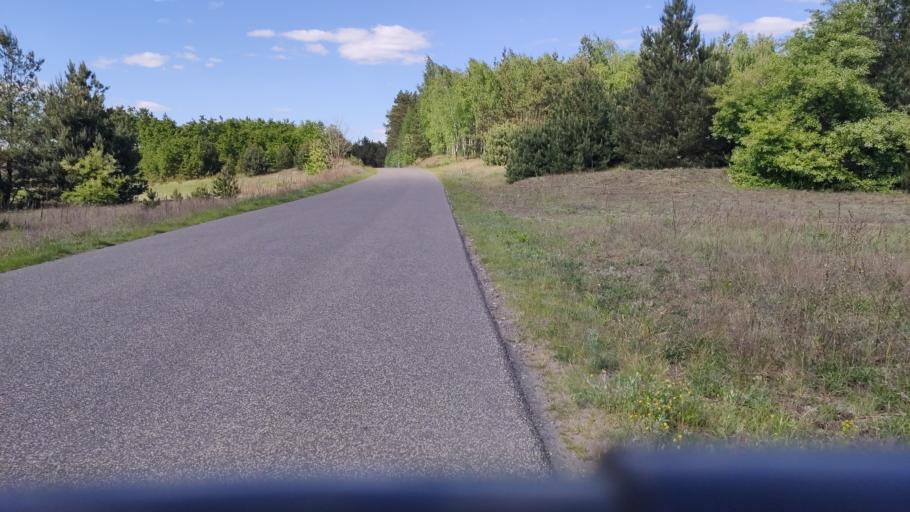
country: PL
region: Kujawsko-Pomorskie
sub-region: Wloclawek
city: Wloclawek
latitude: 52.5876
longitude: 19.0927
